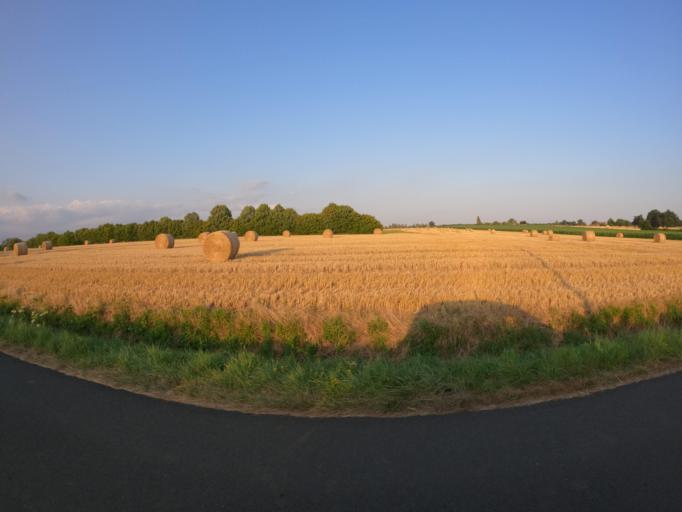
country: FR
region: Pays de la Loire
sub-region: Departement de la Sarthe
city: Brulon
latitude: 47.9284
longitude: -0.2293
